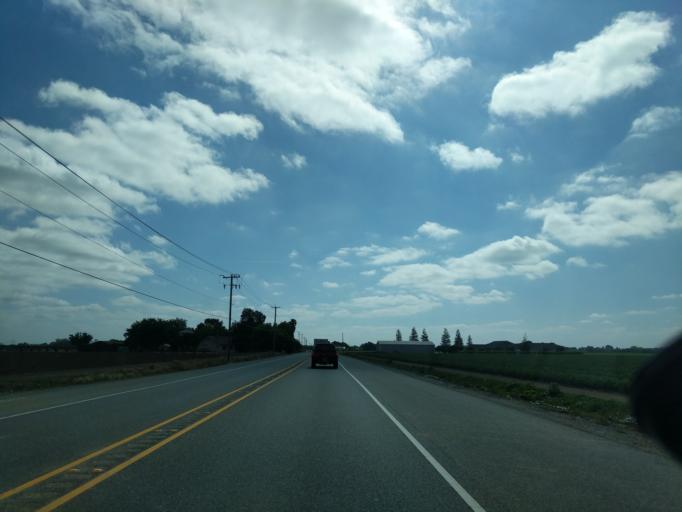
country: US
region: California
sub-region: Contra Costa County
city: Byron
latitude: 37.8965
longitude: -121.6623
